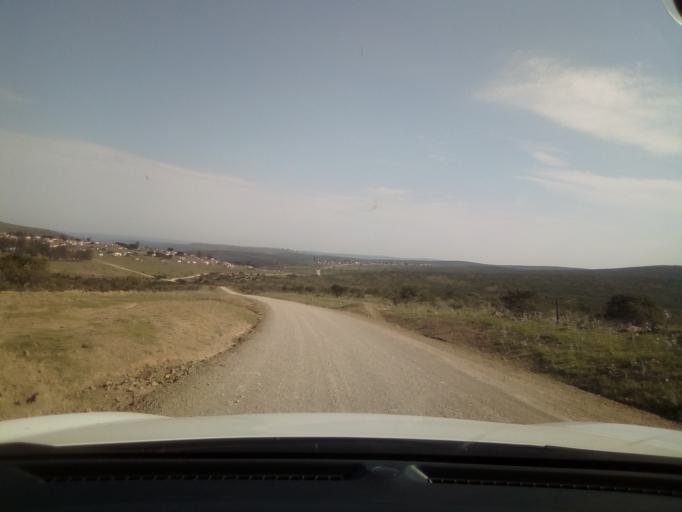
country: ZA
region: Eastern Cape
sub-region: Buffalo City Metropolitan Municipality
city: Bhisho
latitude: -32.9873
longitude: 27.2481
